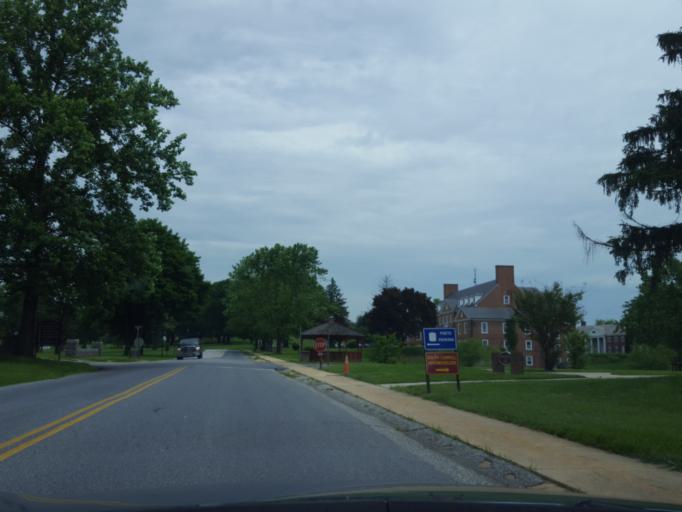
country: US
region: Maryland
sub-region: Carroll County
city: Sykesville
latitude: 39.3823
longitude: -76.9593
